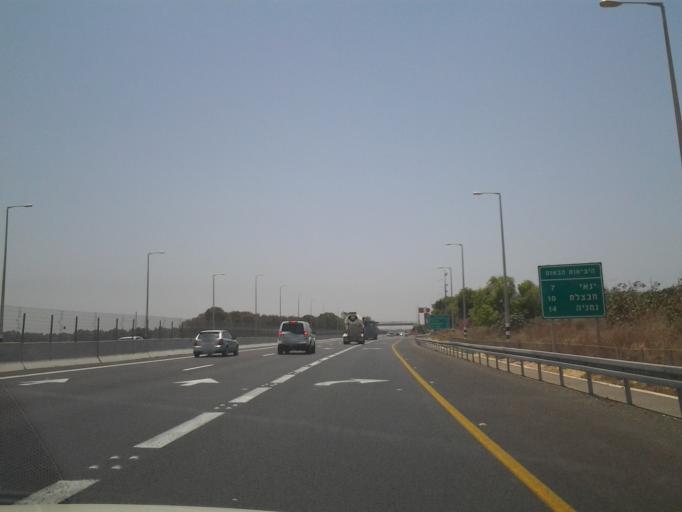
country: IL
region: Haifa
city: Hadera
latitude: 32.4416
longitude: 34.8921
